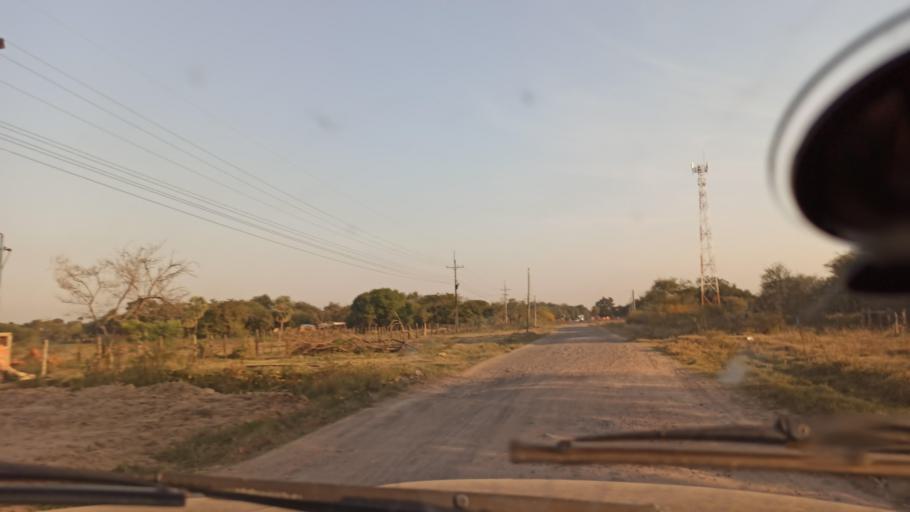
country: PY
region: Presidente Hayes
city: Nanawa
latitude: -25.2310
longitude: -57.6308
